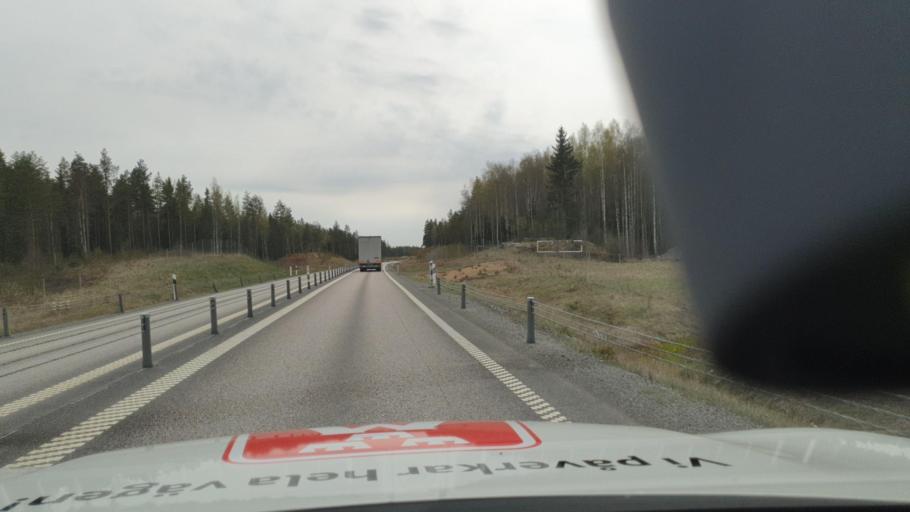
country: SE
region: Uppsala
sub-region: Heby Kommun
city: Tarnsjo
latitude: 60.0840
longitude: 16.9165
